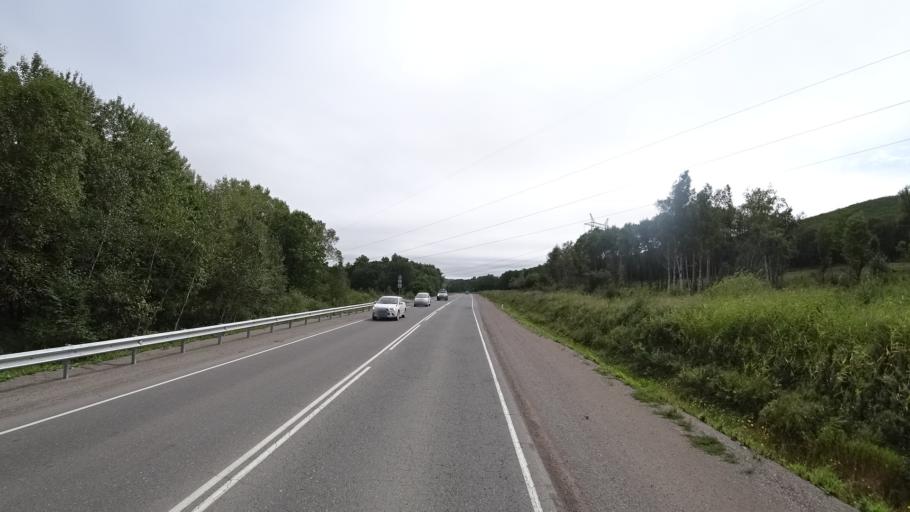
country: RU
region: Primorskiy
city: Lyalichi
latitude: 44.1087
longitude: 132.4204
